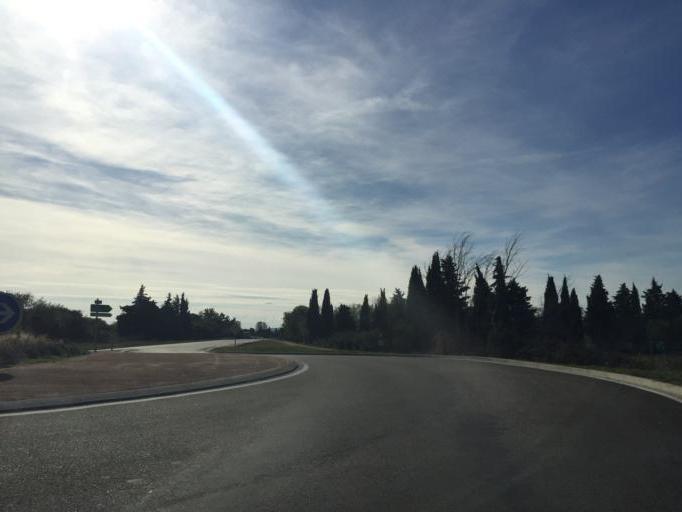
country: FR
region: Rhone-Alpes
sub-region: Departement de la Drome
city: Pierrelatte
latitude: 44.3873
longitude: 4.6982
